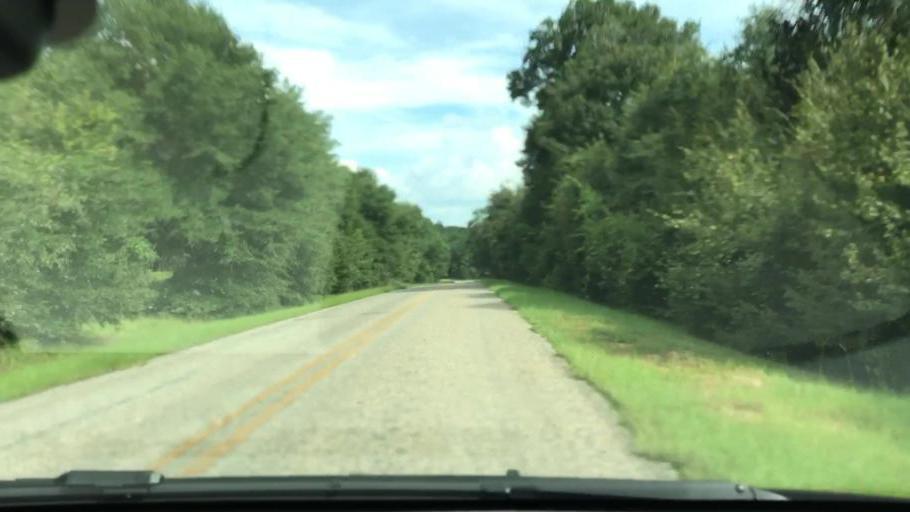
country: US
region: Georgia
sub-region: Early County
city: Blakely
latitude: 31.5057
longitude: -84.9470
